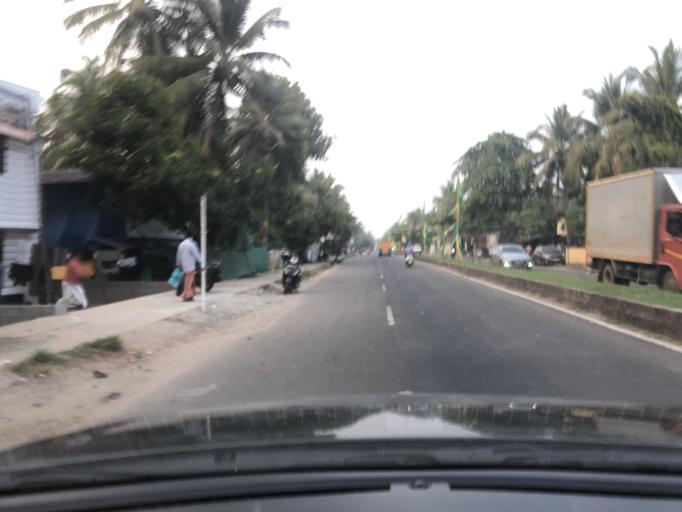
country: IN
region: Kerala
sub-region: Kozhikode
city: Kozhikode
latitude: 11.2948
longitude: 75.7571
